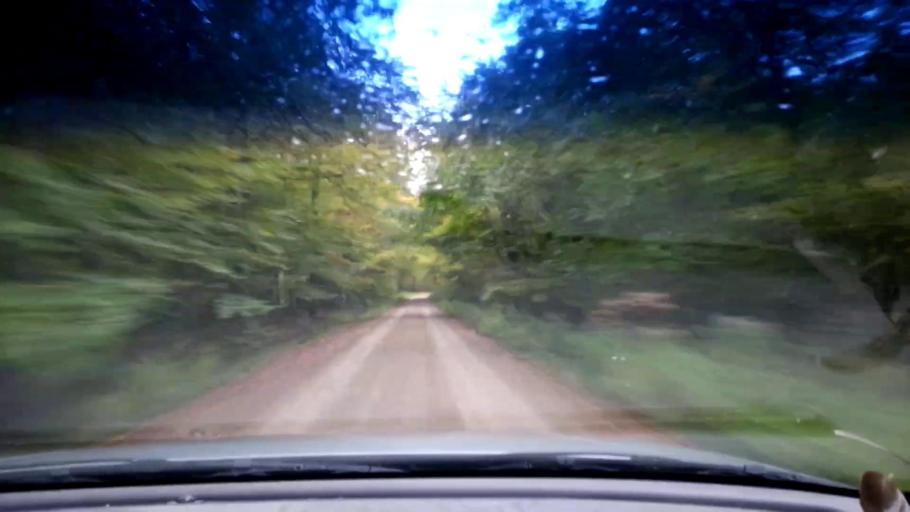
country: DE
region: Bavaria
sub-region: Upper Franconia
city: Burgwindheim
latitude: 49.8353
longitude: 10.6416
